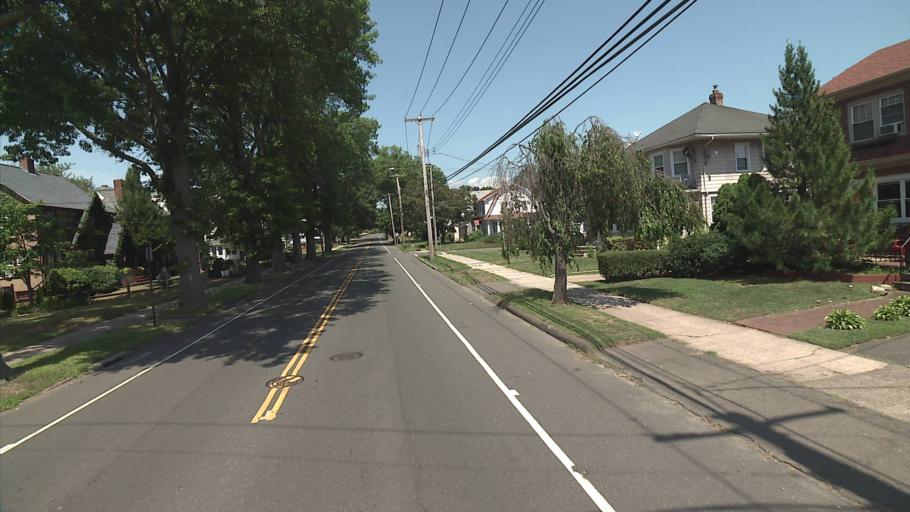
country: US
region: Connecticut
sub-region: New Haven County
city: East Haven
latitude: 41.2702
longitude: -72.8969
